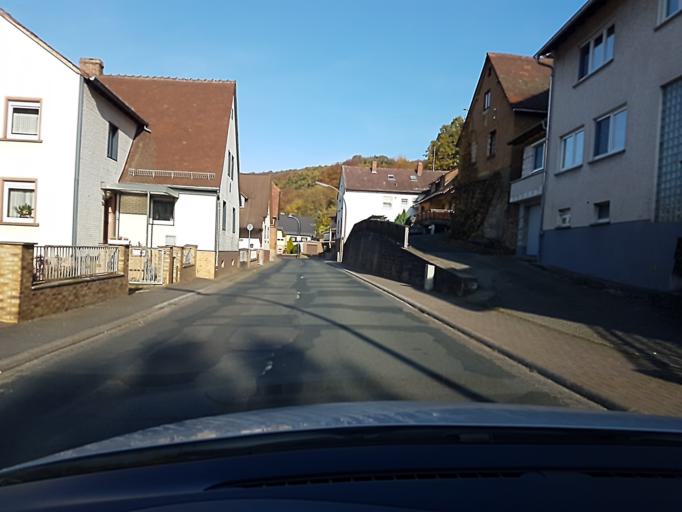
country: DE
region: Bavaria
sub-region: Regierungsbezirk Unterfranken
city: Leidersbach
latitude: 49.8987
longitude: 9.2293
